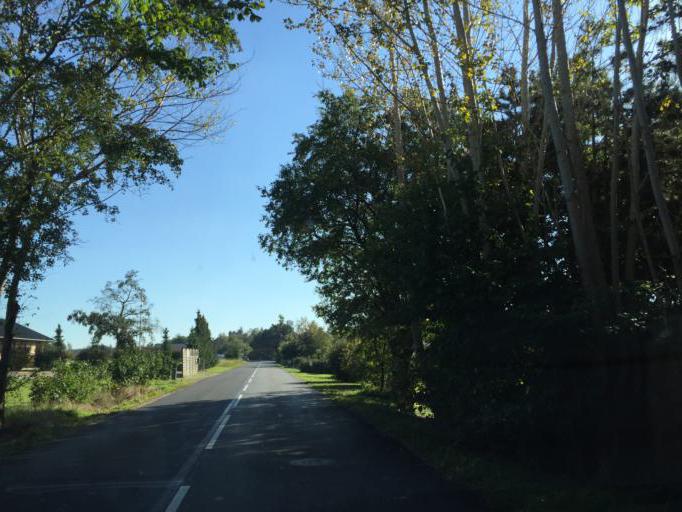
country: DK
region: Zealand
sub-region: Odsherred Kommune
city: Hojby
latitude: 55.9031
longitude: 11.5610
